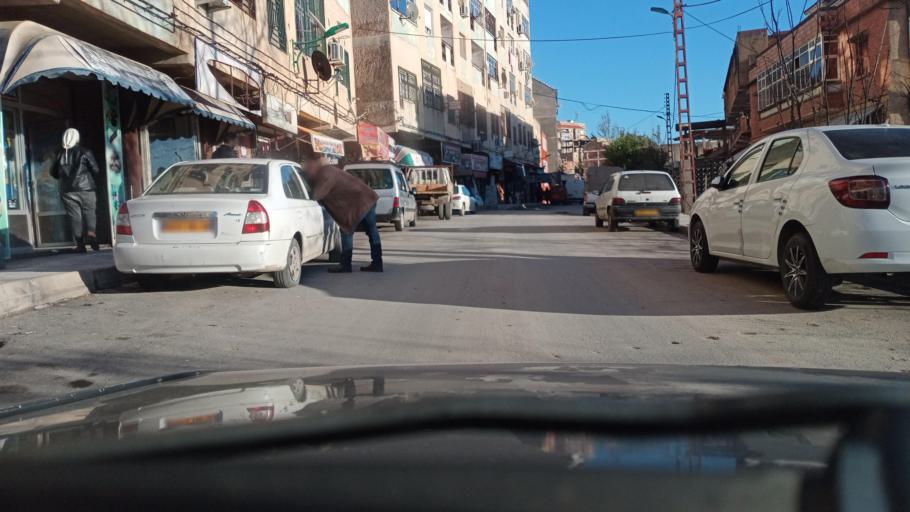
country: DZ
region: Tizi Ouzou
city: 'Ain el Hammam
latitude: 36.5743
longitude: 4.3057
